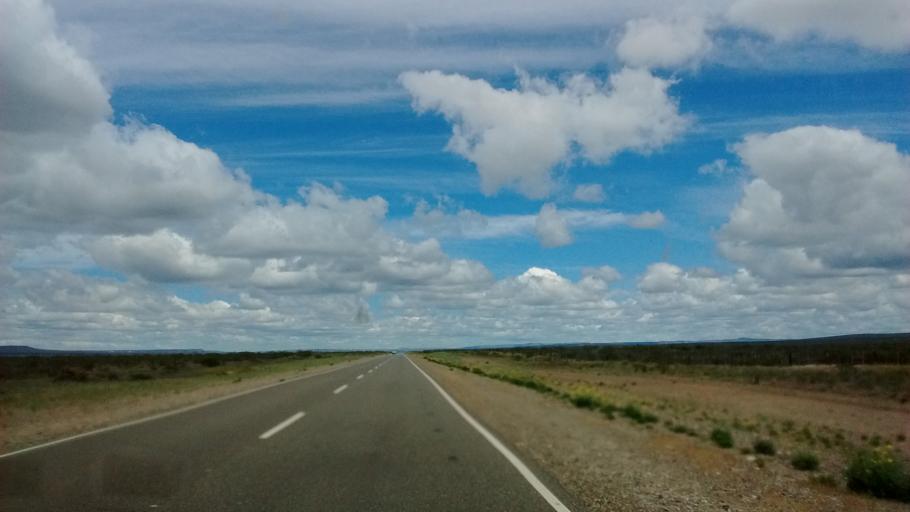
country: AR
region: Neuquen
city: Piedra del Aguila
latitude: -39.8048
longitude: -69.7029
